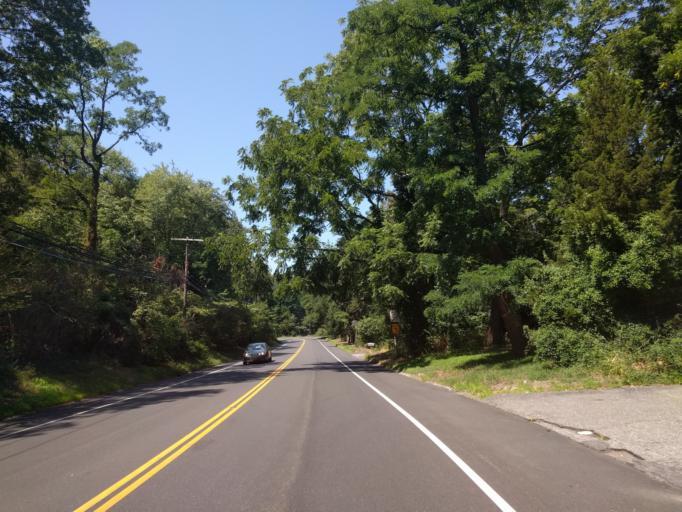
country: US
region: New York
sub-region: Suffolk County
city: Fort Salonga
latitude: 40.9095
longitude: -73.3116
